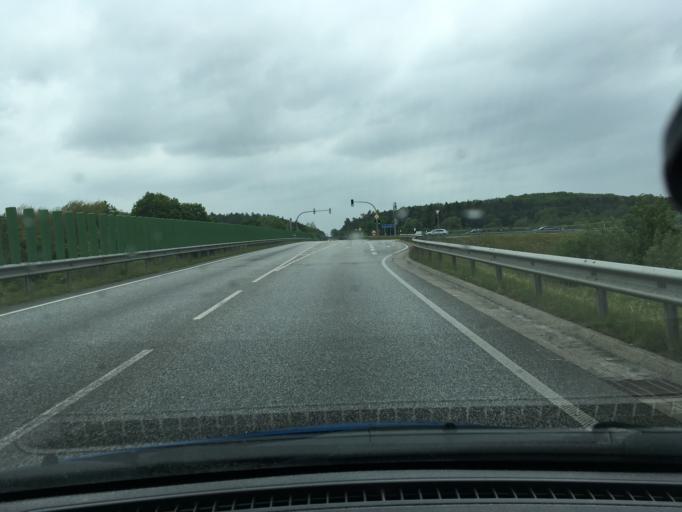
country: DE
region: Schleswig-Holstein
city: Gross Sarau
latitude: 53.7822
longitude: 10.7053
